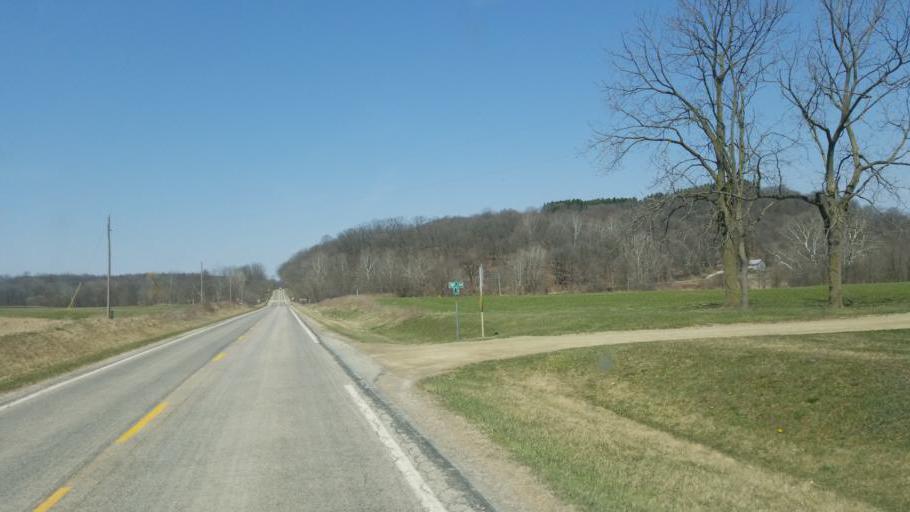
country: US
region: Ohio
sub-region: Ashland County
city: Loudonville
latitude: 40.7109
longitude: -82.1650
